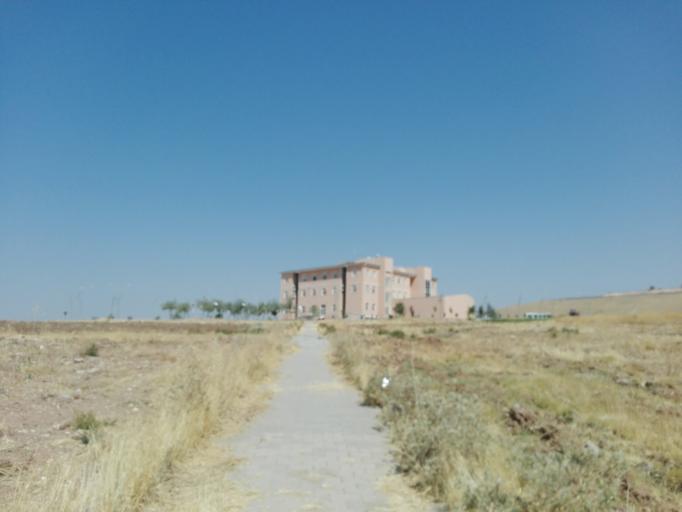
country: TR
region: Batman
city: Oymatas
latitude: 37.7924
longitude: 41.0648
